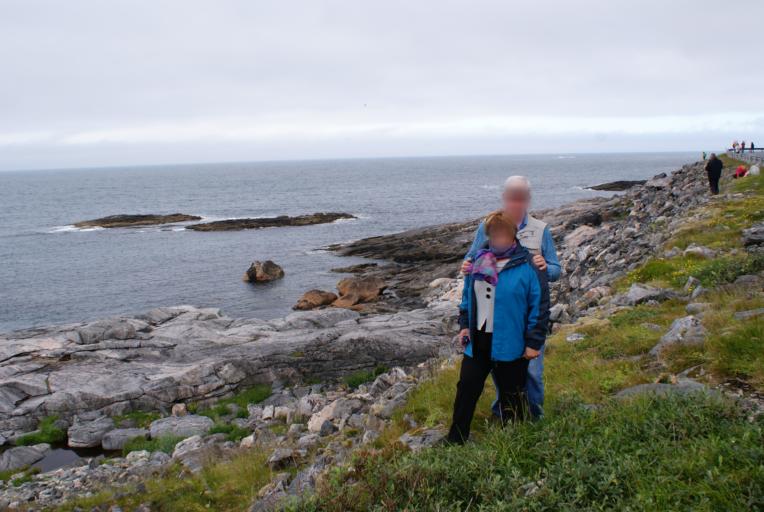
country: NO
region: Nordland
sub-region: Andoy
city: Myre
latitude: 69.0993
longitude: 15.5627
